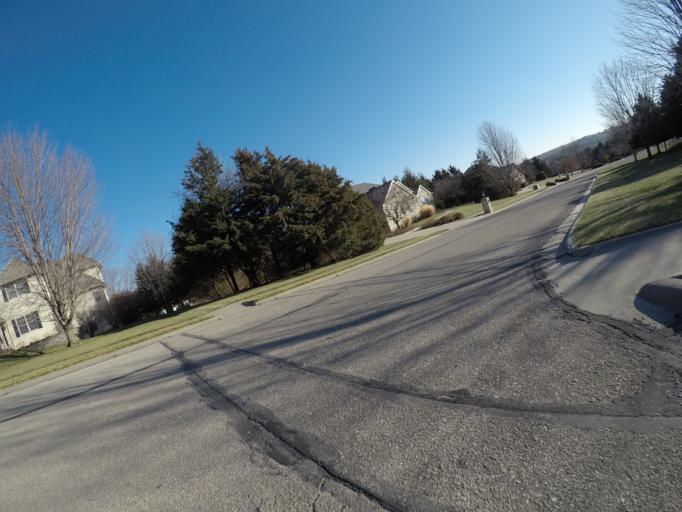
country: US
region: Kansas
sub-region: Riley County
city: Manhattan
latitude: 39.1945
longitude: -96.6361
